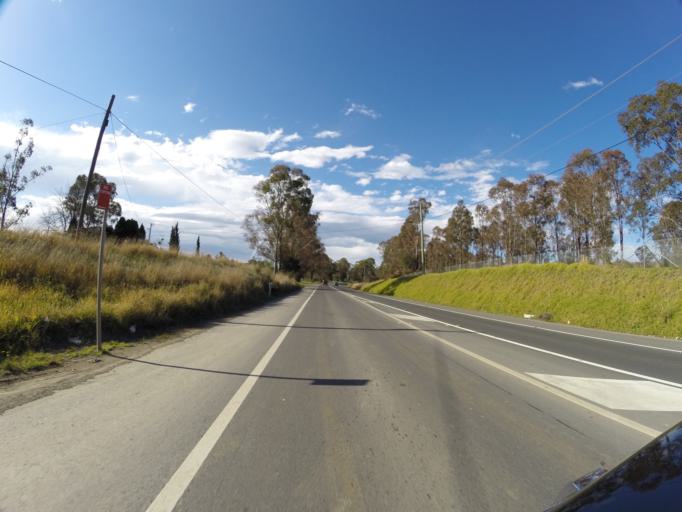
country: AU
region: New South Wales
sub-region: Fairfield
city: Cecil Park
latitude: -33.8765
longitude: 150.8271
